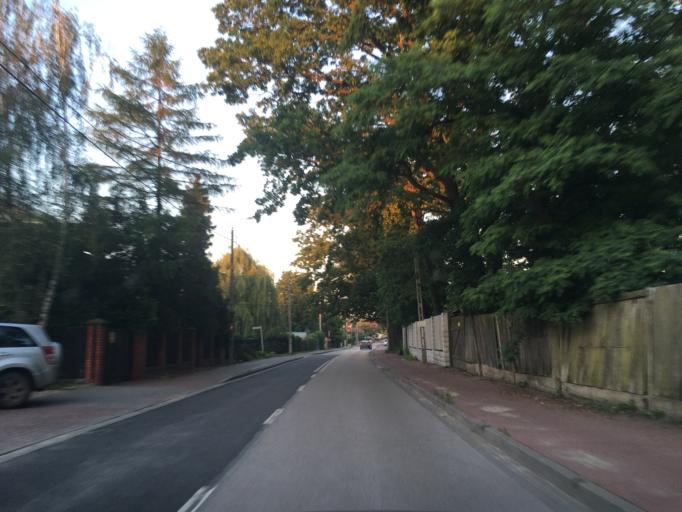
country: PL
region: Masovian Voivodeship
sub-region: Powiat piaseczynski
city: Piaseczno
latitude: 52.0639
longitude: 21.0126
